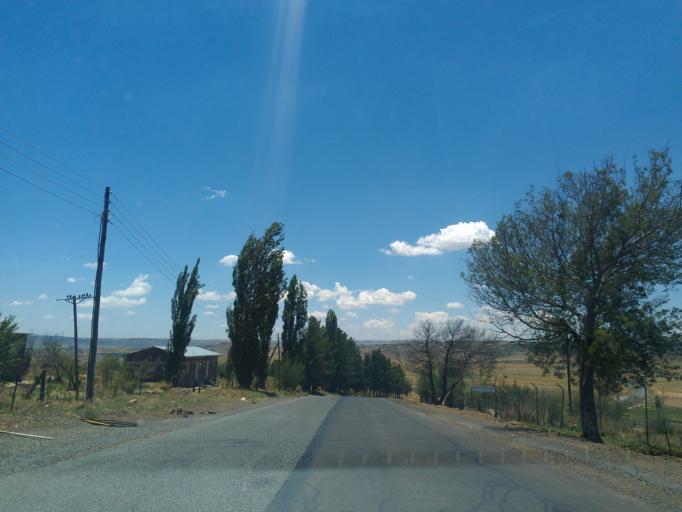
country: LS
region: Berea
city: Teyateyaneng
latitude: -29.1367
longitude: 27.7676
